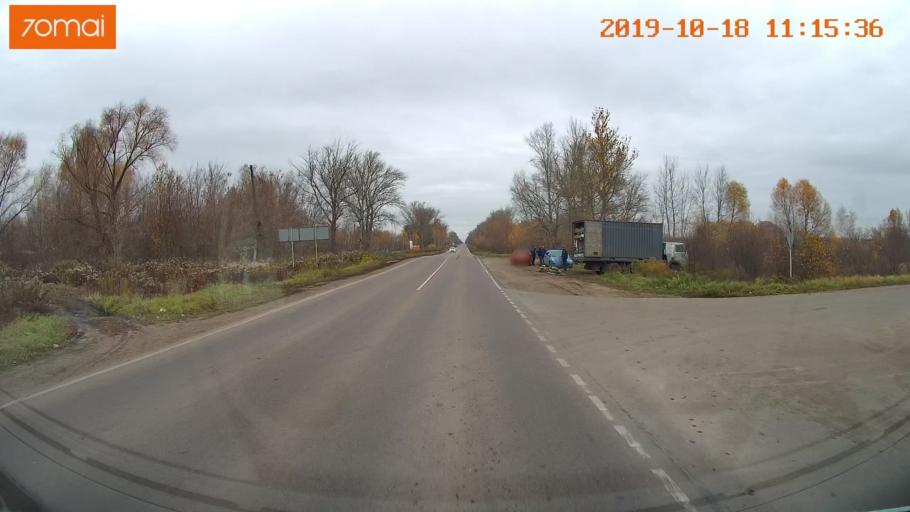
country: RU
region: Tula
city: Kimovsk
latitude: 53.9945
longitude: 38.5476
